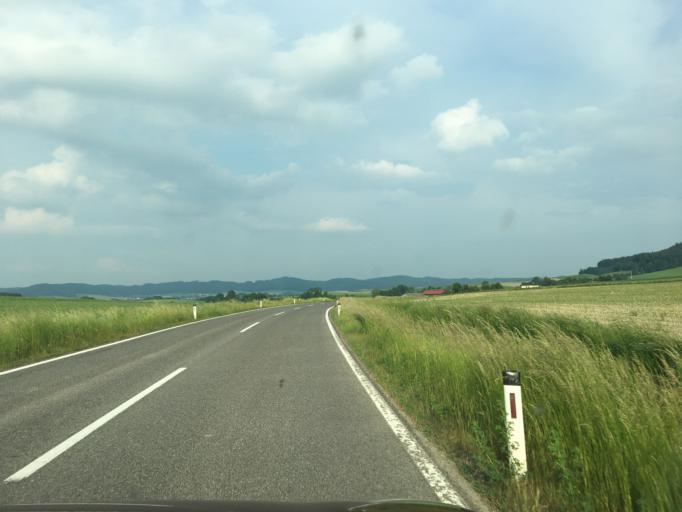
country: AT
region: Upper Austria
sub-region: Politischer Bezirk Ried im Innkreis
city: Ried im Innkreis
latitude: 48.1506
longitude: 13.5163
